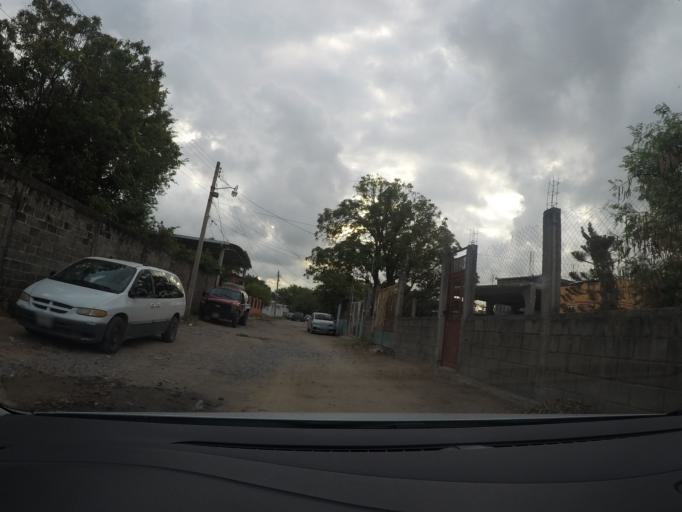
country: MX
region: Oaxaca
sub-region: Salina Cruz
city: Salina Cruz
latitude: 16.2099
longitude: -95.1985
